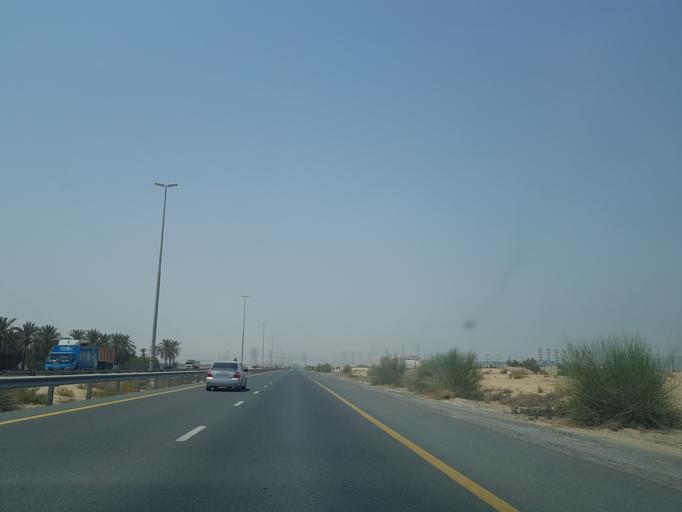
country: AE
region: Ash Shariqah
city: Sharjah
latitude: 25.1525
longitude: 55.4452
